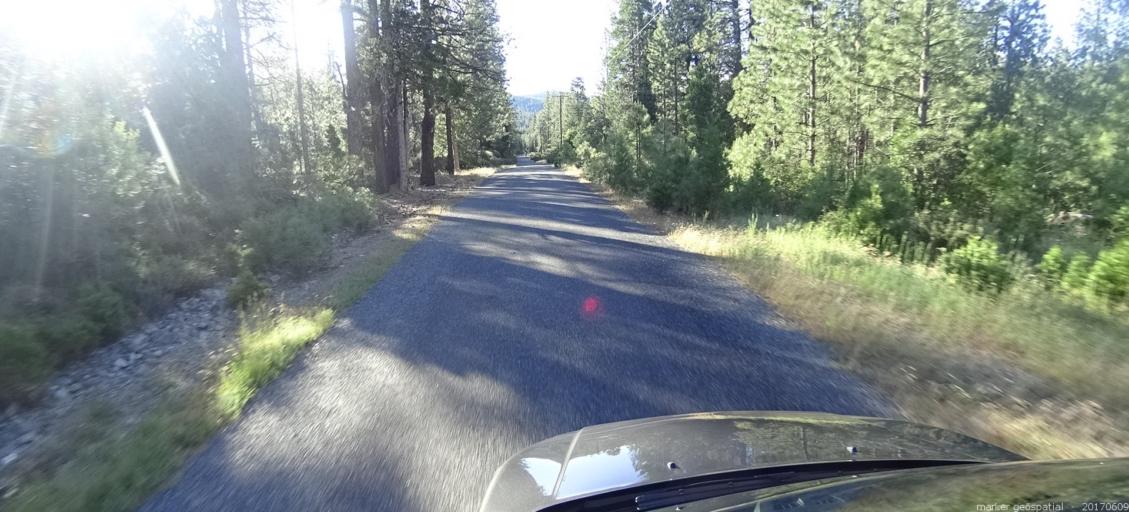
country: US
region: California
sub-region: Siskiyou County
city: Weed
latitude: 41.3817
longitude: -122.6683
